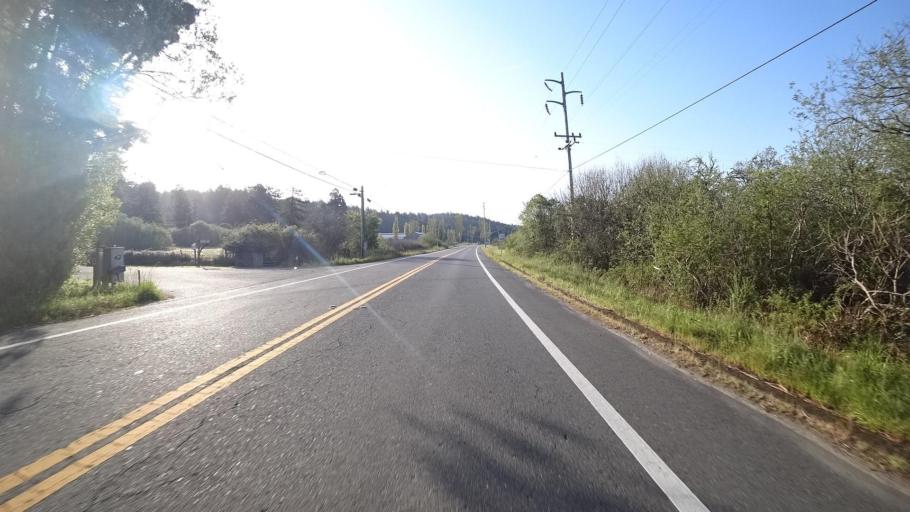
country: US
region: California
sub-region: Humboldt County
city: Myrtletown
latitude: 40.7842
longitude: -124.0812
